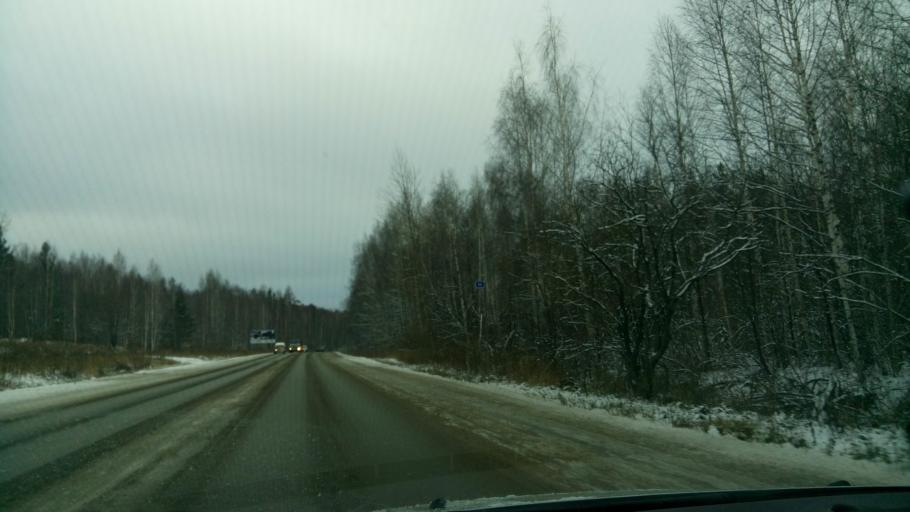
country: RU
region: Sverdlovsk
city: Polevskoy
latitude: 56.4660
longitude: 60.2247
